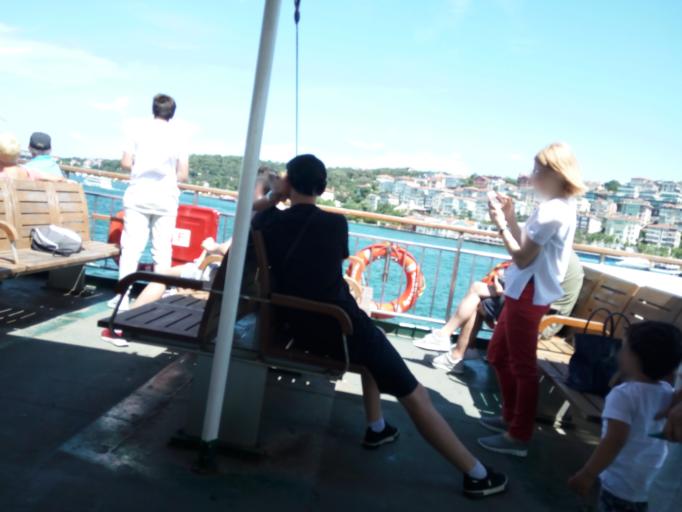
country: TR
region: Istanbul
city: UEskuedar
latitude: 41.0311
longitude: 29.0143
